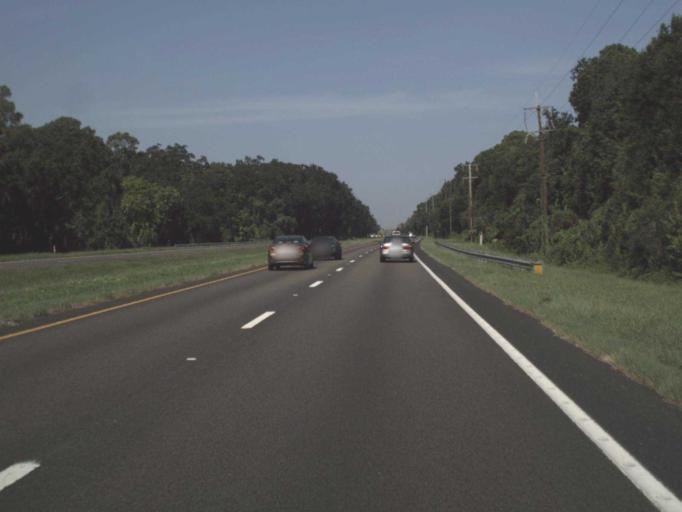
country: US
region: Florida
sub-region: Hillsborough County
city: Valrico
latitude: 27.9377
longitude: -82.1926
